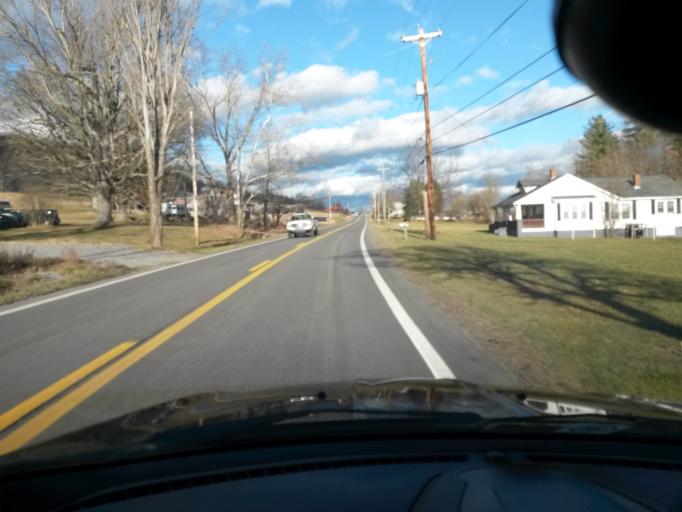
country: US
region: Virginia
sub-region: Giles County
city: Pearisburg
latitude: 37.4098
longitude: -80.7549
